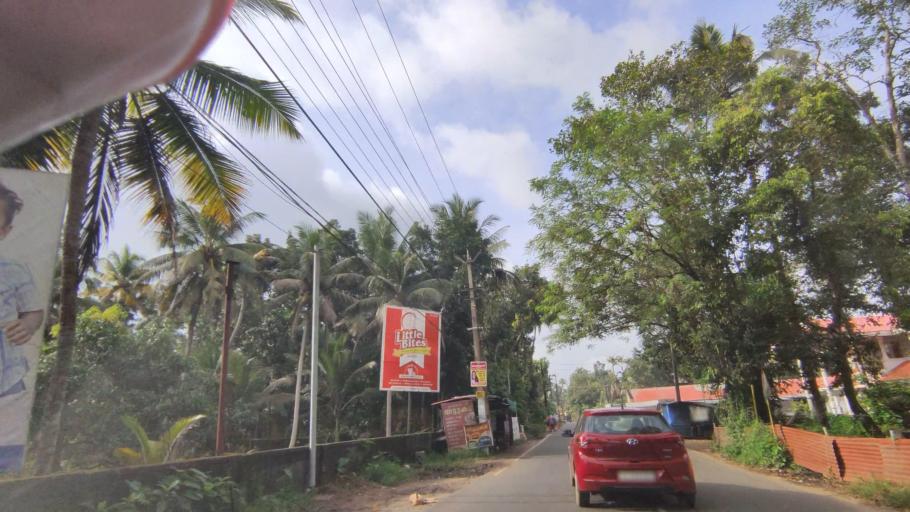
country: IN
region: Kerala
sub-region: Kottayam
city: Kottayam
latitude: 9.5913
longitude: 76.4880
